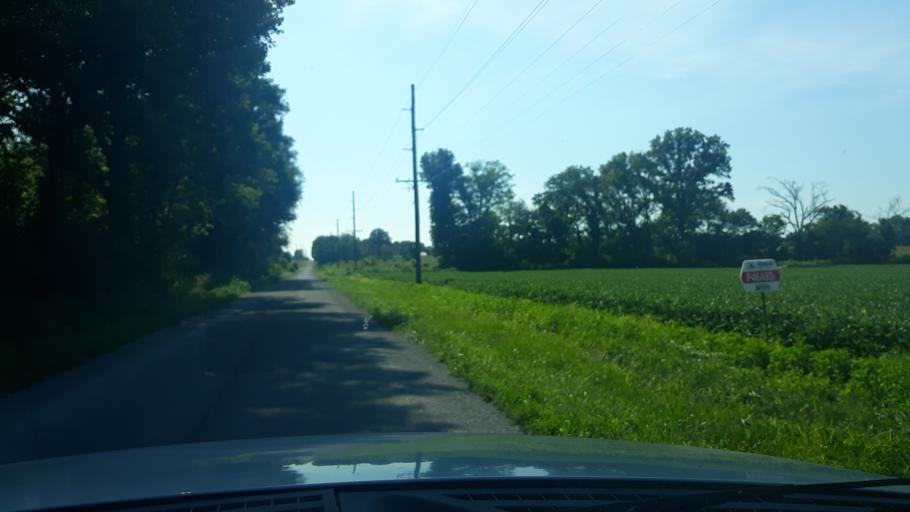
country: US
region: Illinois
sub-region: Saline County
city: Eldorado
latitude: 37.8630
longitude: -88.5249
